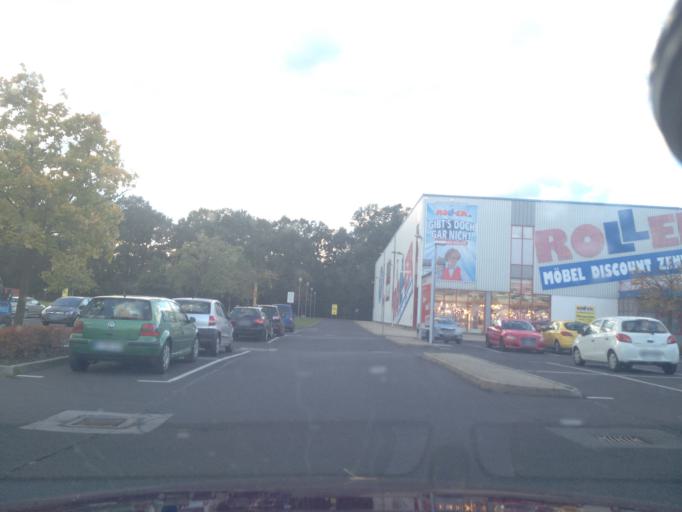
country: DE
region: Saxony
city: Goerlitz
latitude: 51.1699
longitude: 14.9666
